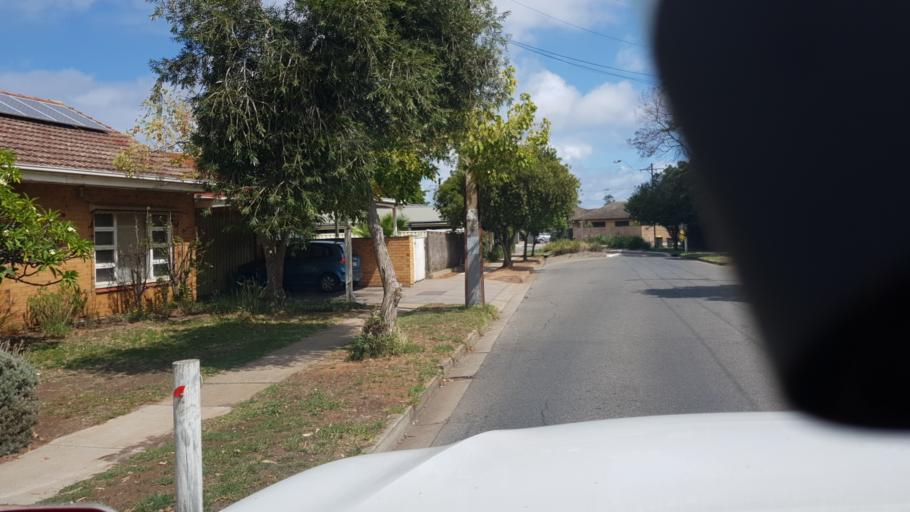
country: AU
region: South Australia
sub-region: Adelaide
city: Brighton
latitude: -35.0155
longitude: 138.5287
